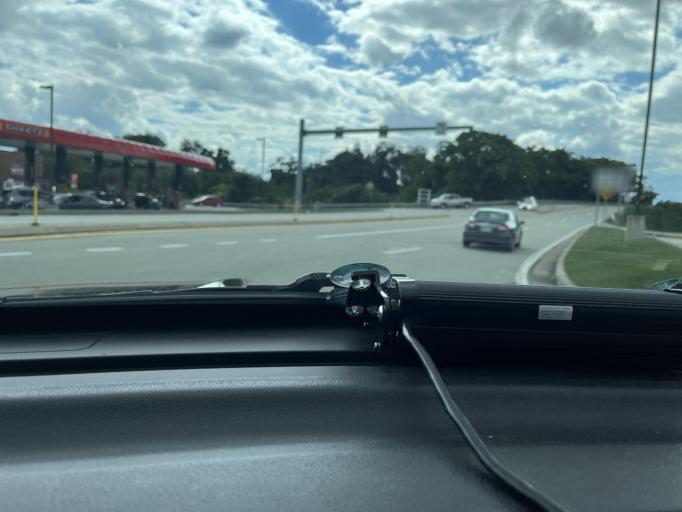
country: US
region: Pennsylvania
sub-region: Fayette County
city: South Uniontown
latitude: 39.9118
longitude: -79.7472
